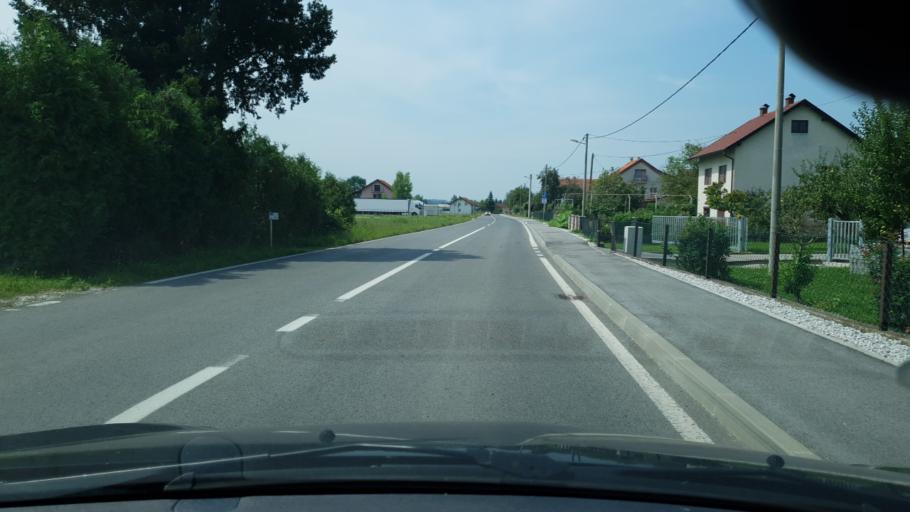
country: HR
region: Krapinsko-Zagorska
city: Bedekovcina
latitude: 46.0320
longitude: 15.9690
